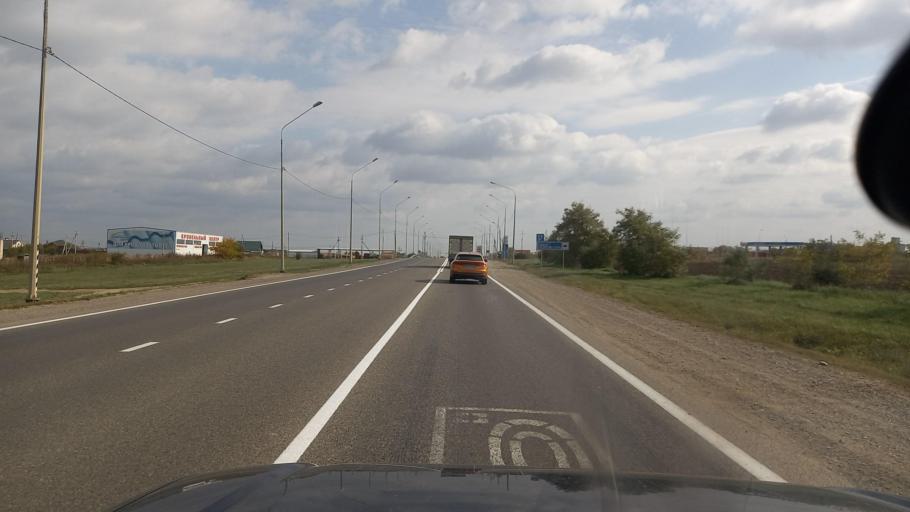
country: RU
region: Krasnodarskiy
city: Il'skiy
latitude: 44.8463
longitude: 38.5461
